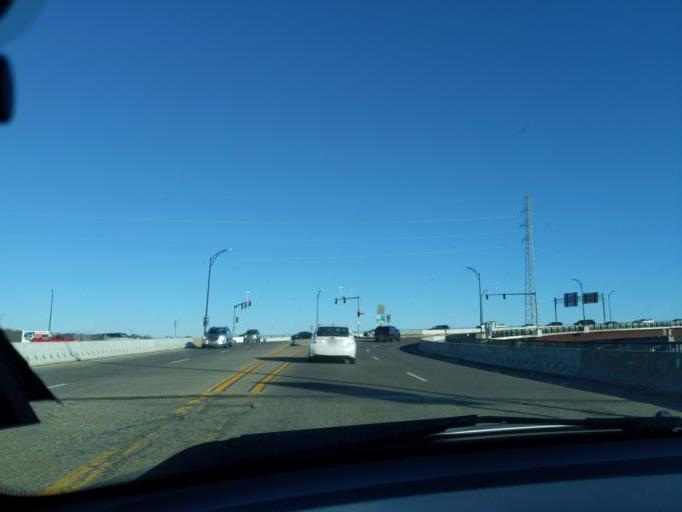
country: US
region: Massachusetts
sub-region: Essex County
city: Salem
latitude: 42.5363
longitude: -70.8874
